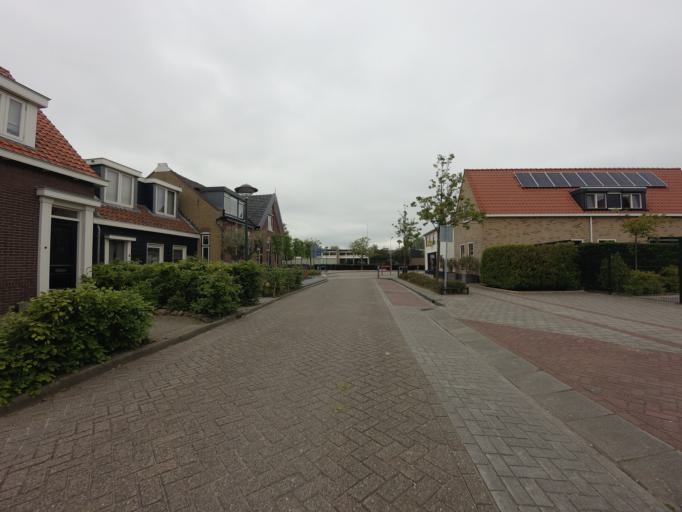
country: NL
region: South Holland
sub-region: Gemeente Spijkenisse
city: Spijkenisse
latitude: 51.8124
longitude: 4.3383
